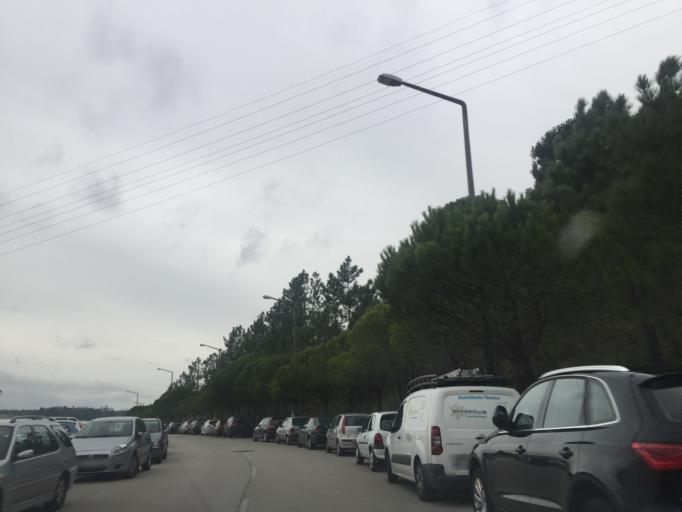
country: PT
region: Coimbra
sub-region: Coimbra
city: Coimbra
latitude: 40.1869
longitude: -8.4148
